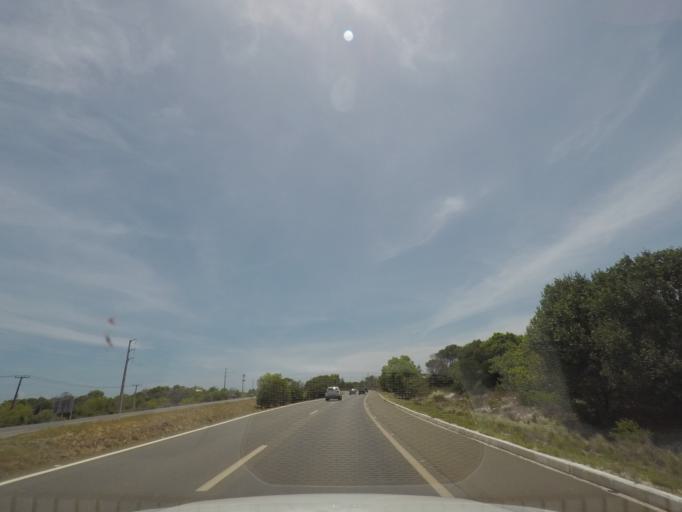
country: BR
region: Bahia
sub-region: Mata De Sao Joao
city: Mata de Sao Joao
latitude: -12.6153
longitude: -38.0552
